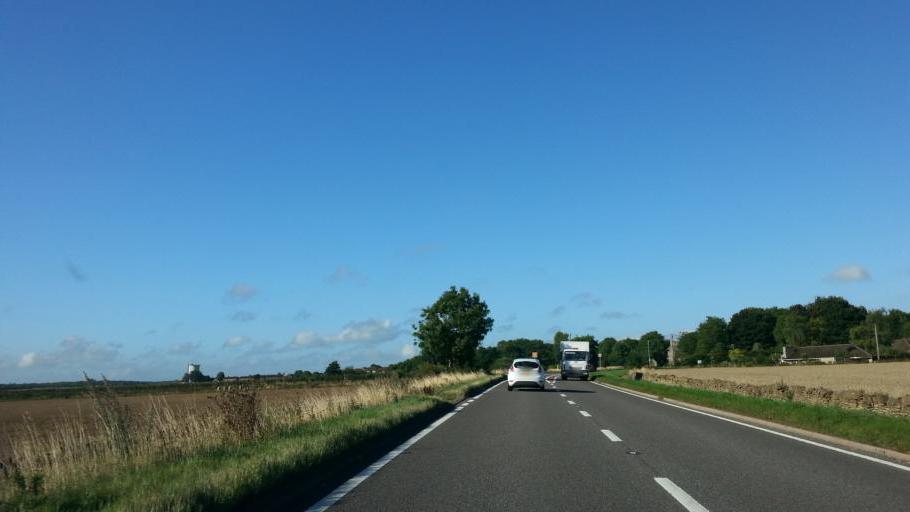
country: GB
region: England
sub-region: District of Rutland
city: Tinwell
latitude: 52.6184
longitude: -0.5211
